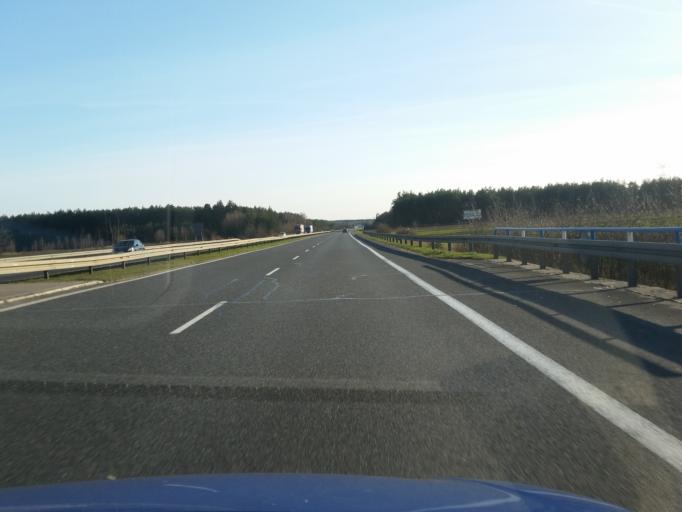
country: PL
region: Lodz Voivodeship
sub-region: Powiat radomszczanski
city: Radomsko
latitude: 51.0656
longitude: 19.3648
